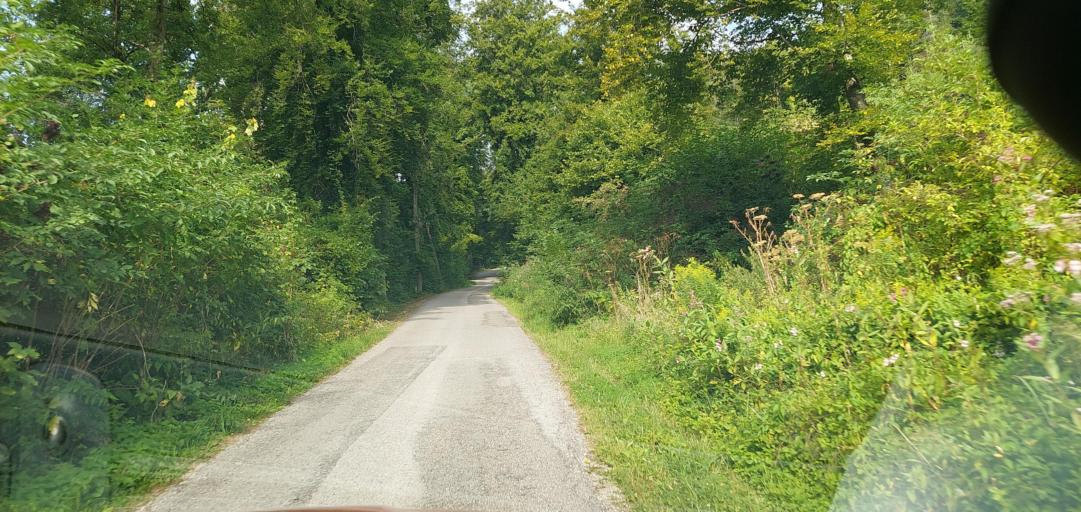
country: AT
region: Upper Austria
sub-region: Politischer Bezirk Urfahr-Umgebung
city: Feldkirchen an der Donau
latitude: 48.3246
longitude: 13.9893
